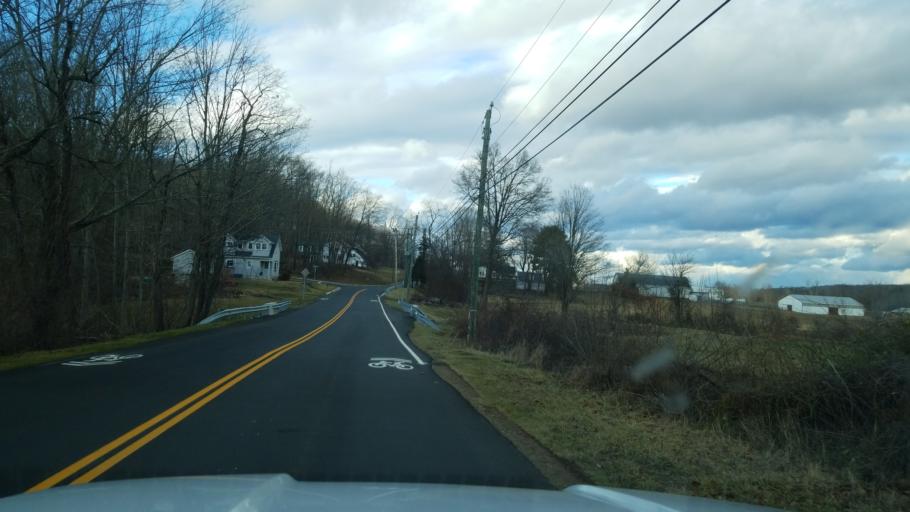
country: US
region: Connecticut
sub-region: Middlesex County
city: Middletown
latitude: 41.5116
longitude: -72.6345
